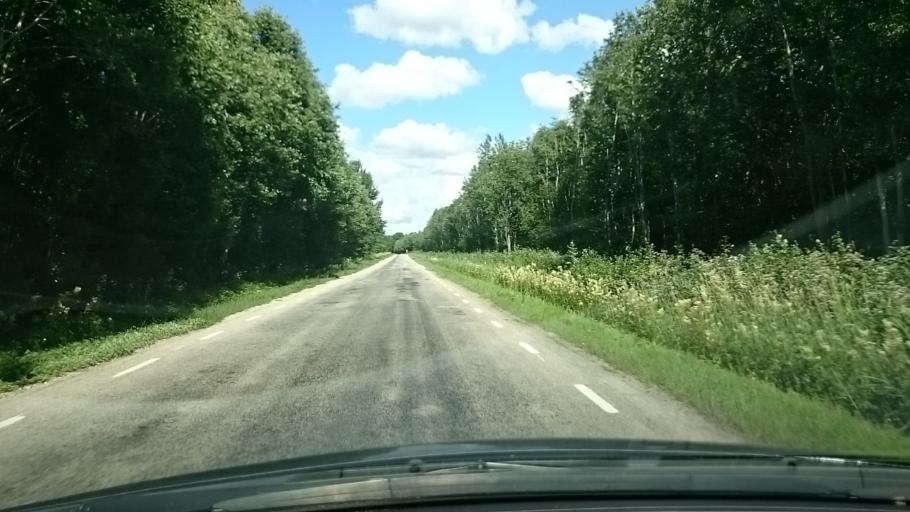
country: EE
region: Laeaene
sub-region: Haapsalu linn
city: Haapsalu
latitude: 59.0645
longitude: 23.5745
